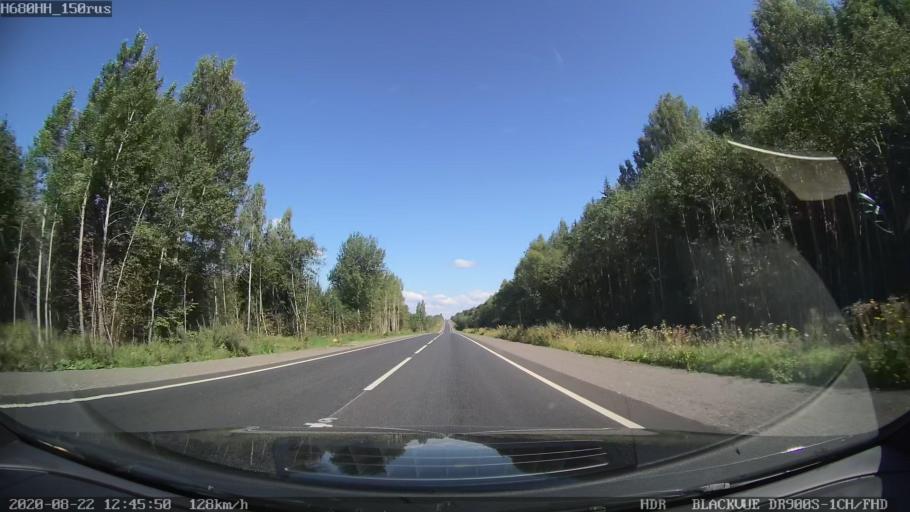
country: RU
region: Tverskaya
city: Rameshki
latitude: 57.4106
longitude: 36.1305
